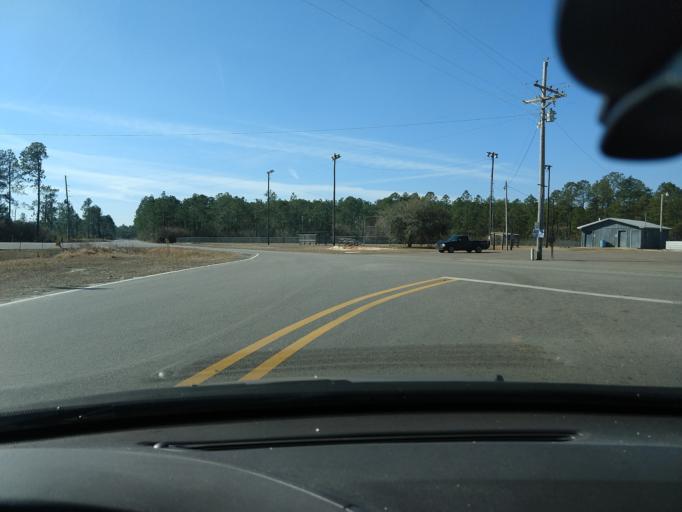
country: US
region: Alabama
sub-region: Mobile County
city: Grand Bay
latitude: 30.4965
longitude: -88.4149
